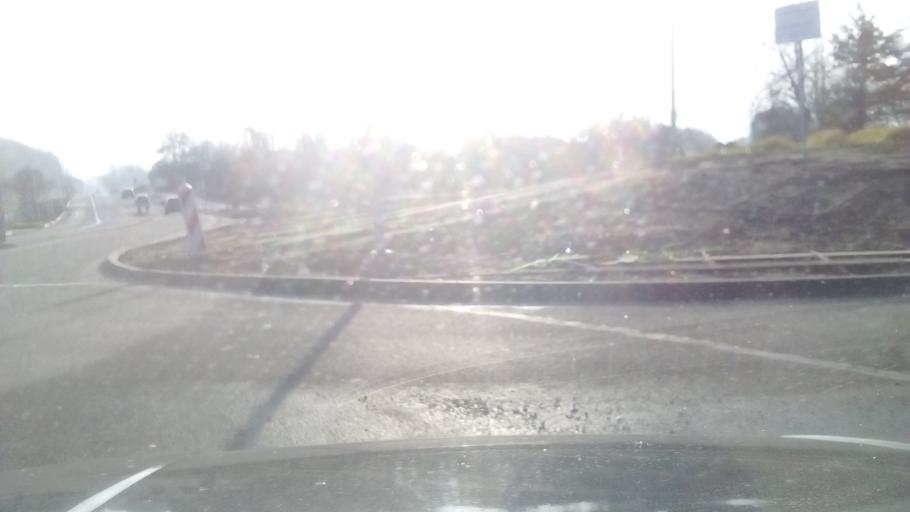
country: LT
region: Alytaus apskritis
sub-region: Alytus
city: Alytus
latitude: 54.4093
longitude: 24.0047
